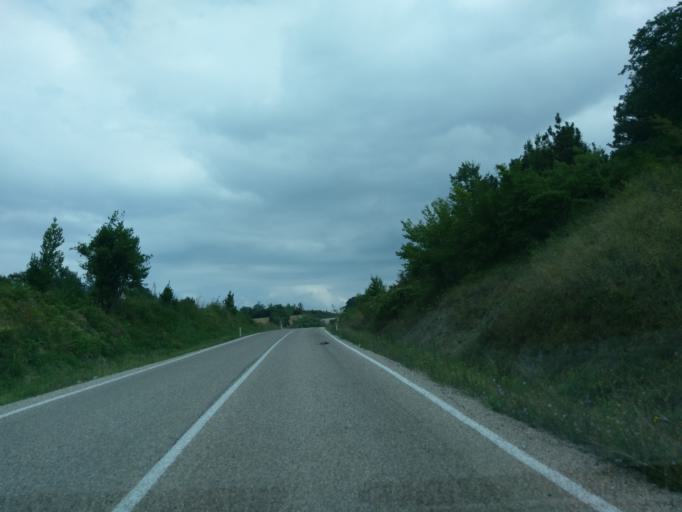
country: TR
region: Sinop
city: Erfelek
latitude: 41.9661
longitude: 34.8357
